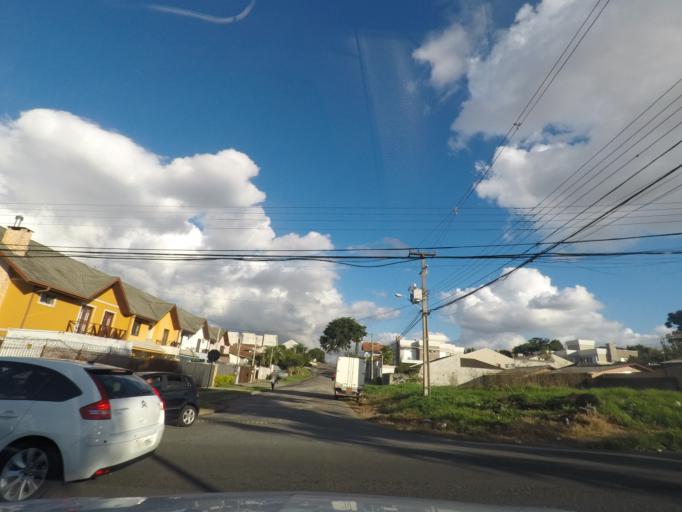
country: BR
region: Parana
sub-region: Sao Jose Dos Pinhais
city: Sao Jose dos Pinhais
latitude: -25.4917
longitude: -49.2577
